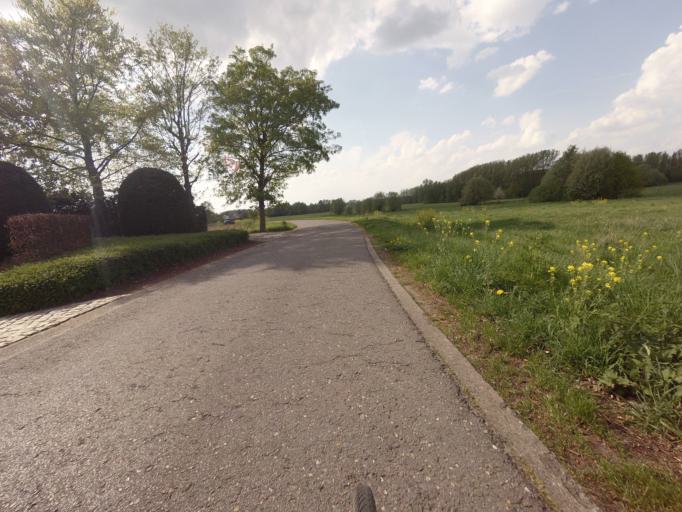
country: BE
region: Flanders
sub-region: Provincie Antwerpen
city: Putte
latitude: 51.0649
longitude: 4.6675
